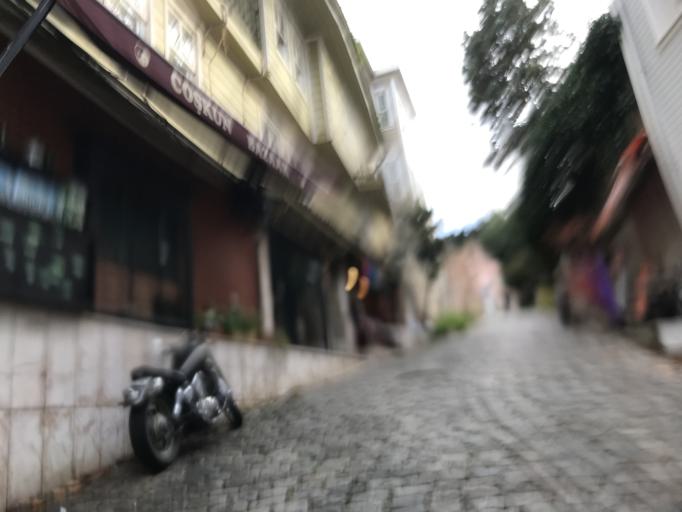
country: TR
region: Istanbul
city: Eminoenue
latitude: 41.0104
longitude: 28.9792
